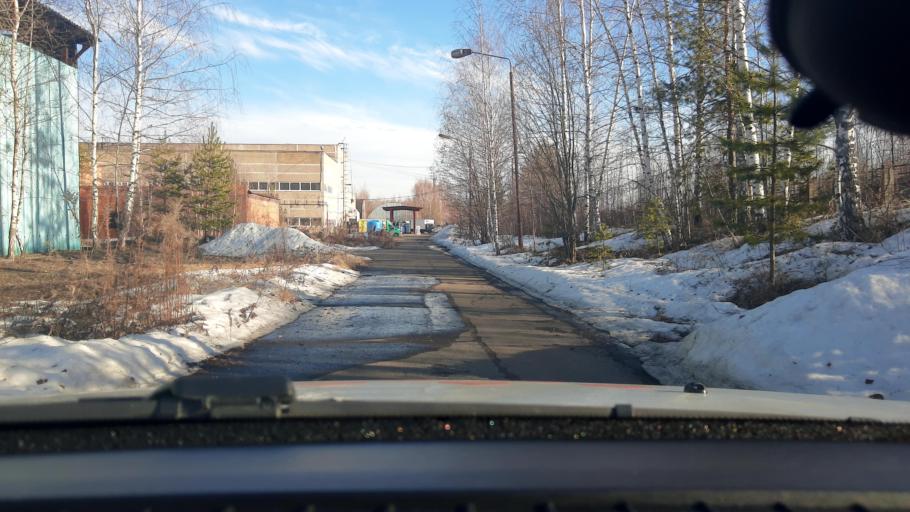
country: RU
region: Nizjnij Novgorod
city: Afonino
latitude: 56.2176
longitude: 44.0592
